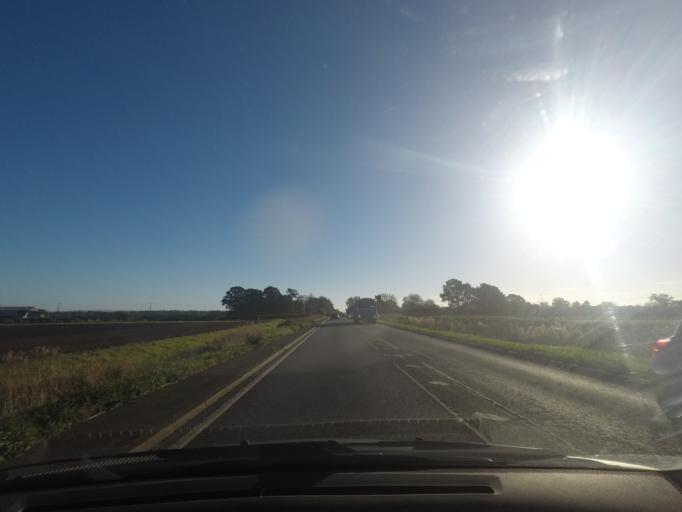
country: GB
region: England
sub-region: City of York
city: Holtby
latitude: 53.9537
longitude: -0.9630
